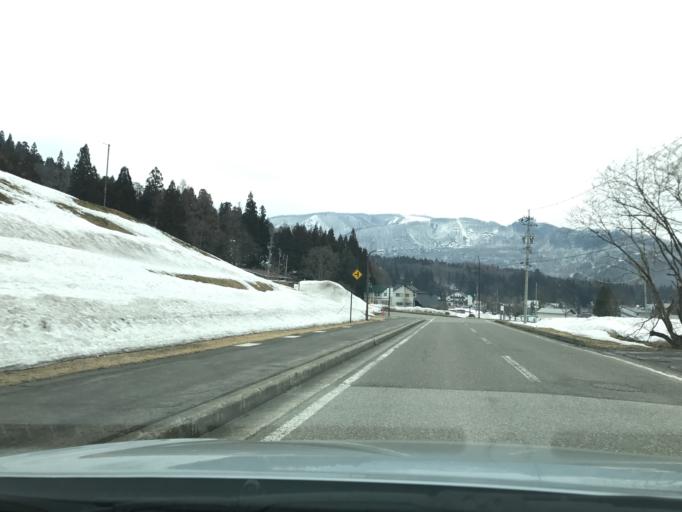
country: JP
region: Nagano
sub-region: Kitaazumi Gun
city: Hakuba
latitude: 36.6953
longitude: 137.8384
